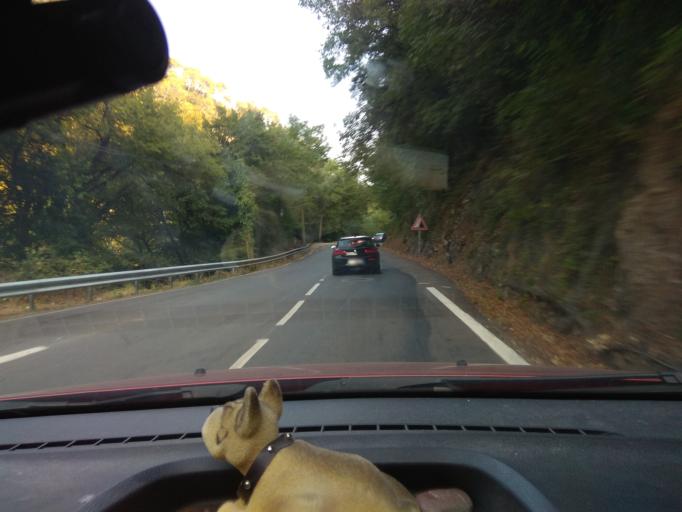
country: FR
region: Provence-Alpes-Cote d'Azur
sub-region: Departement des Alpes-Maritimes
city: La Colle-sur-Loup
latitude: 43.6833
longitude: 7.0738
